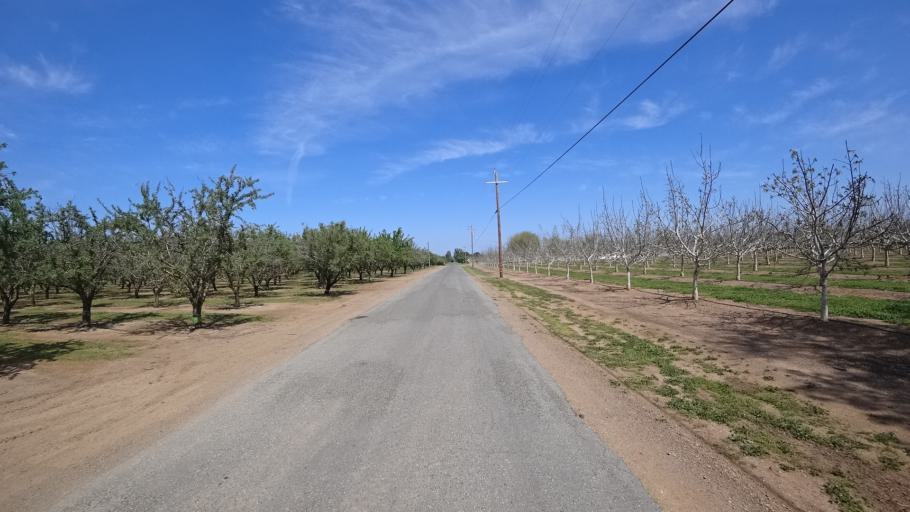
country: US
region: California
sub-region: Glenn County
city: Hamilton City
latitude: 39.8015
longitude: -122.0664
